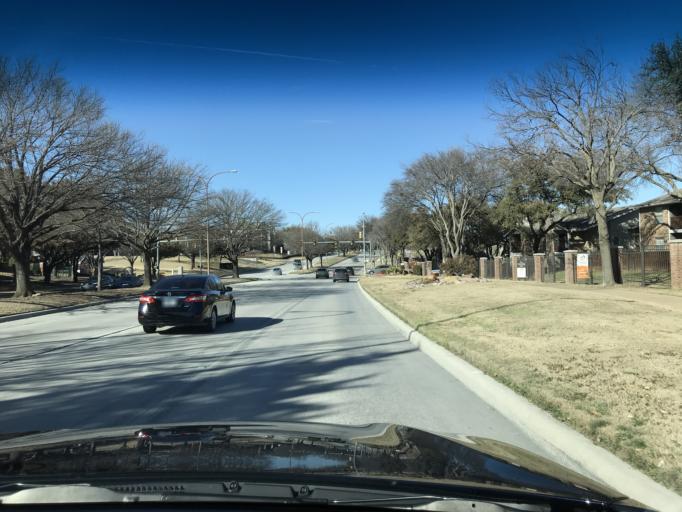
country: US
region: Texas
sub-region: Tarrant County
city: Benbrook
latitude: 32.6711
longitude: -97.4191
